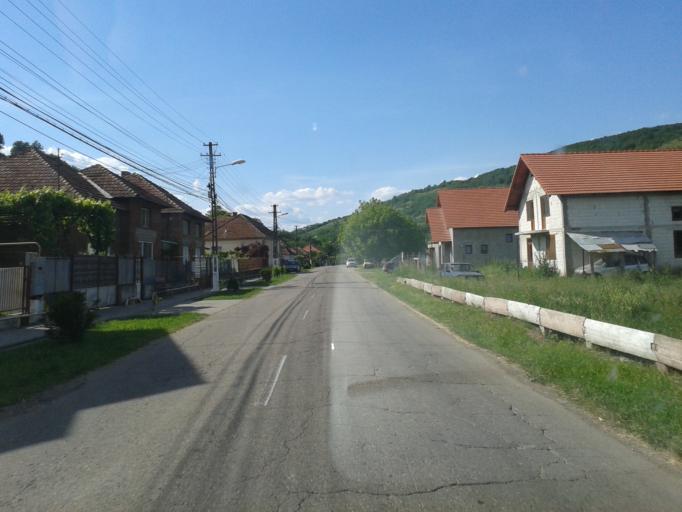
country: RO
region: Hunedoara
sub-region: Comuna Geoagiu
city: Geoagiu
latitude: 45.9319
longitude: 23.1949
